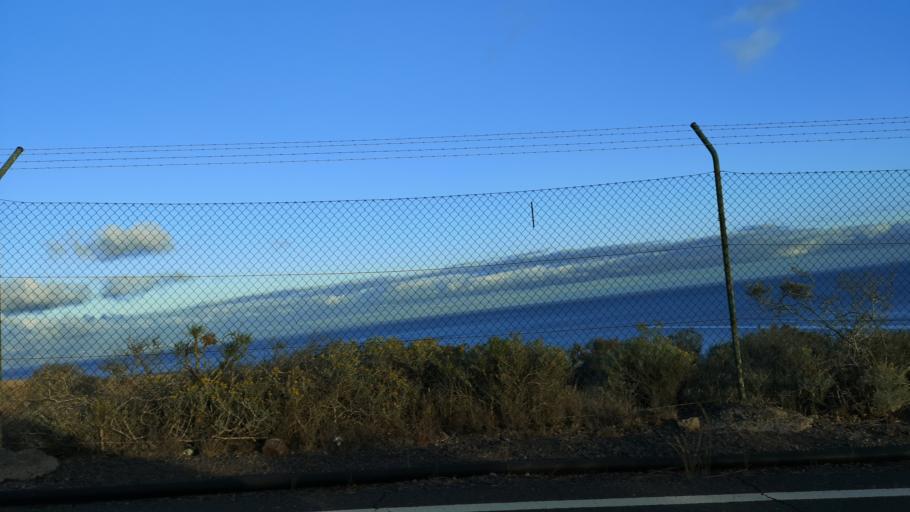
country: ES
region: Canary Islands
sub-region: Provincia de Santa Cruz de Tenerife
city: Alajero
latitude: 28.0293
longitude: -17.2059
